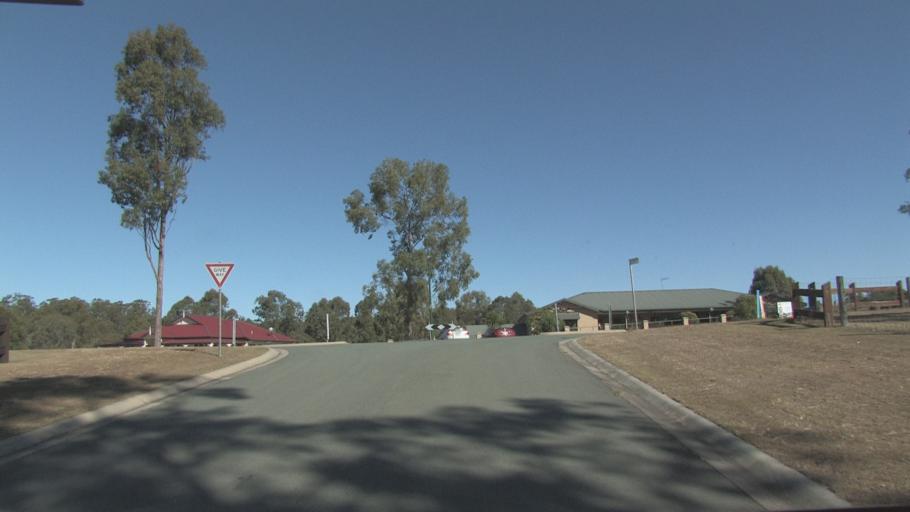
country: AU
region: Queensland
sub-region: Logan
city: Cedar Vale
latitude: -27.8714
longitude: 153.0381
